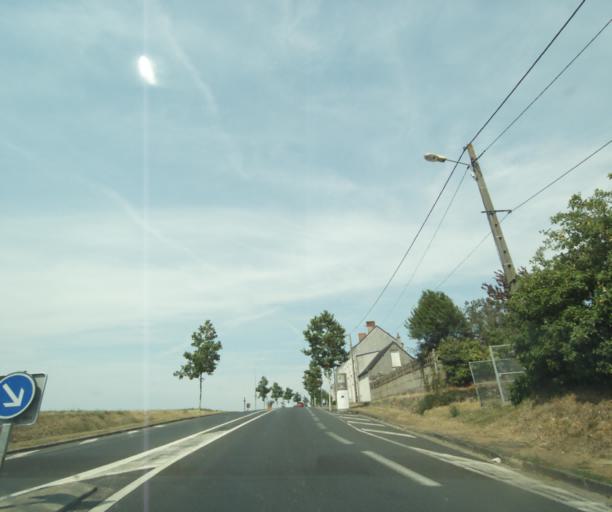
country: FR
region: Centre
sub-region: Departement d'Indre-et-Loire
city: Sainte-Maure-de-Touraine
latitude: 47.1173
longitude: 0.6200
